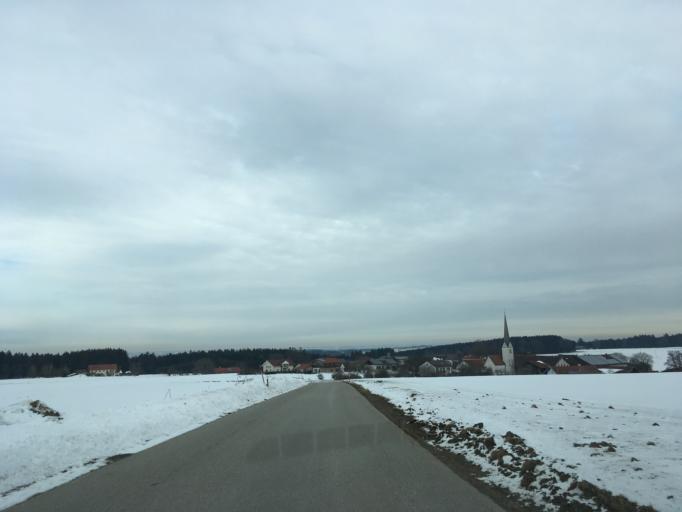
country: DE
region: Bavaria
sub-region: Upper Bavaria
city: Unterreit
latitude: 48.1083
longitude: 12.3712
